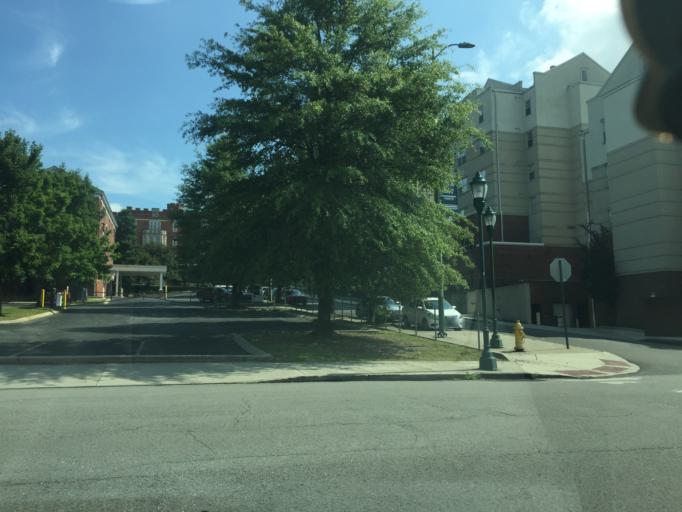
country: US
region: Tennessee
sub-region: Hamilton County
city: Chattanooga
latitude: 35.0441
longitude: -85.2996
